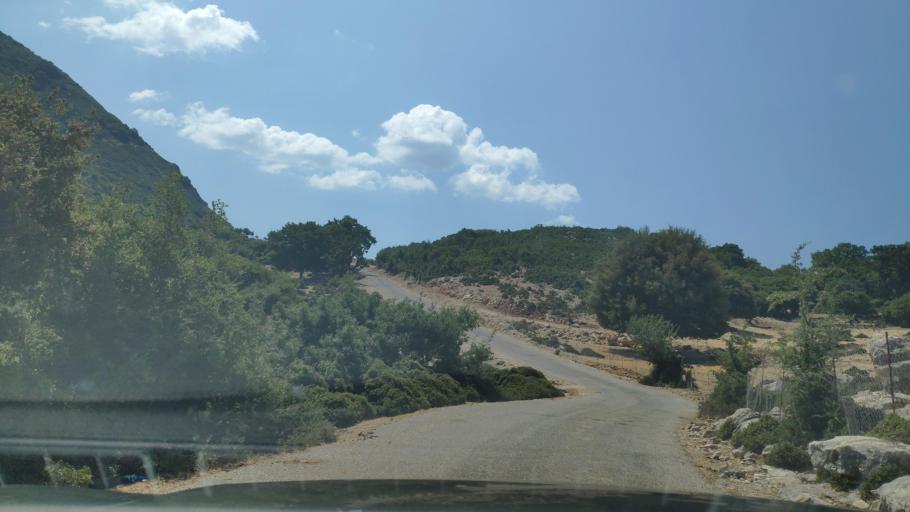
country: GR
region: West Greece
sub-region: Nomos Aitolias kai Akarnanias
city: Monastirakion
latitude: 38.8196
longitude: 20.9331
